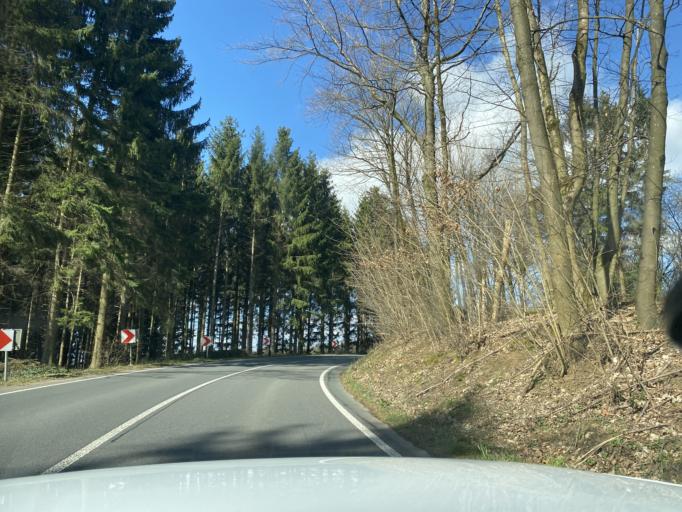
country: DE
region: North Rhine-Westphalia
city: Radevormwald
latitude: 51.2500
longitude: 7.3519
